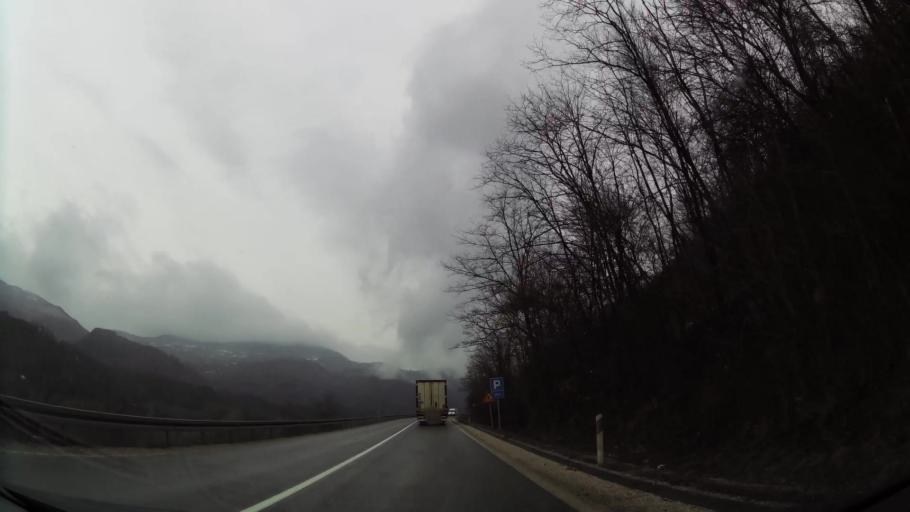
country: RS
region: Central Serbia
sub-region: Pcinjski Okrug
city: Vladicin Han
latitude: 42.7922
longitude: 22.0939
